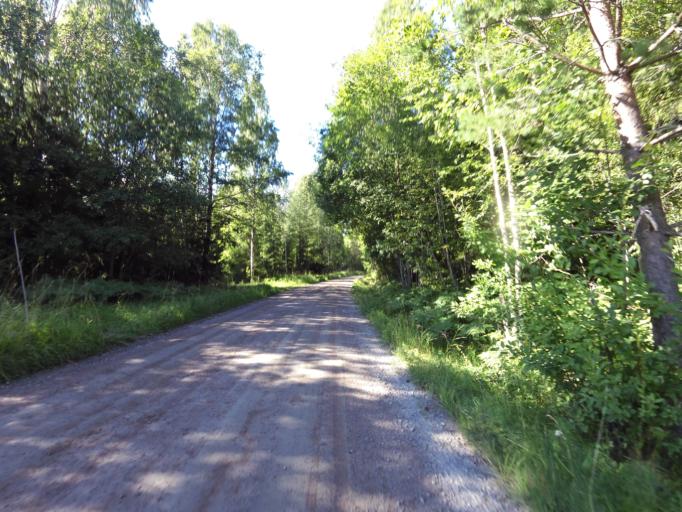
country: SE
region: Gaevleborg
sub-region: Hofors Kommun
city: Hofors
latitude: 60.5333
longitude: 16.4112
